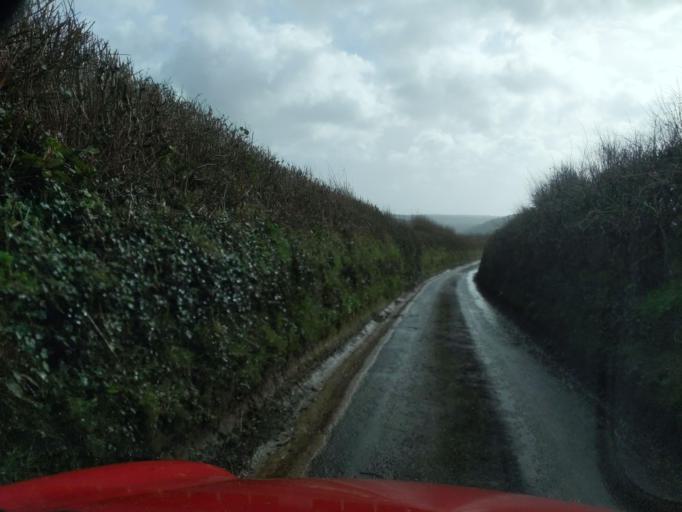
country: GB
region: England
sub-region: Devon
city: Ivybridge
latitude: 50.3598
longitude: -3.9289
